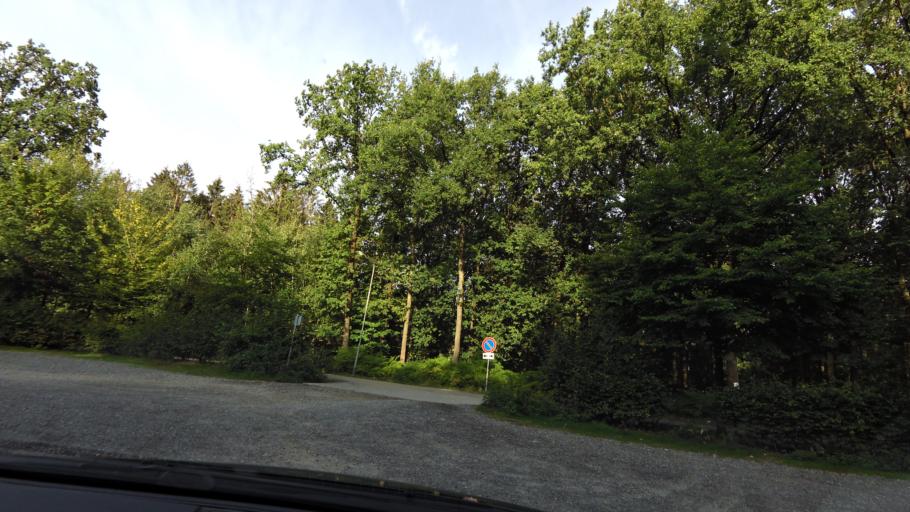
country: BE
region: Wallonia
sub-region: Province de Liege
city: Plombieres
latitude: 50.7725
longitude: 5.9630
